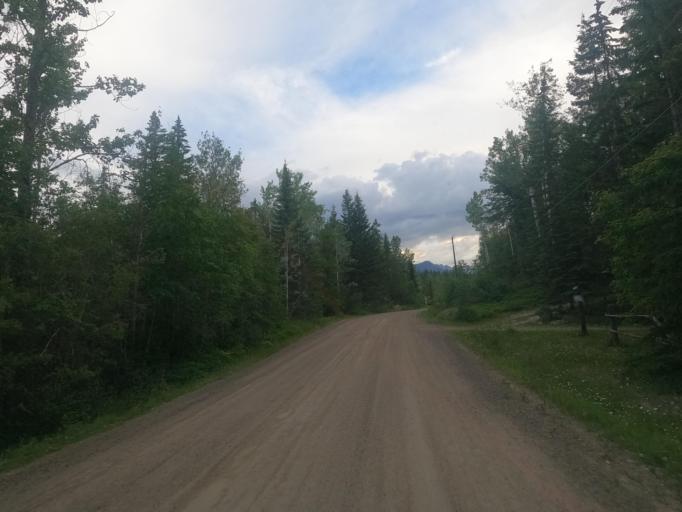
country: CA
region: British Columbia
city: Golden
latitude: 51.4480
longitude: -117.0069
